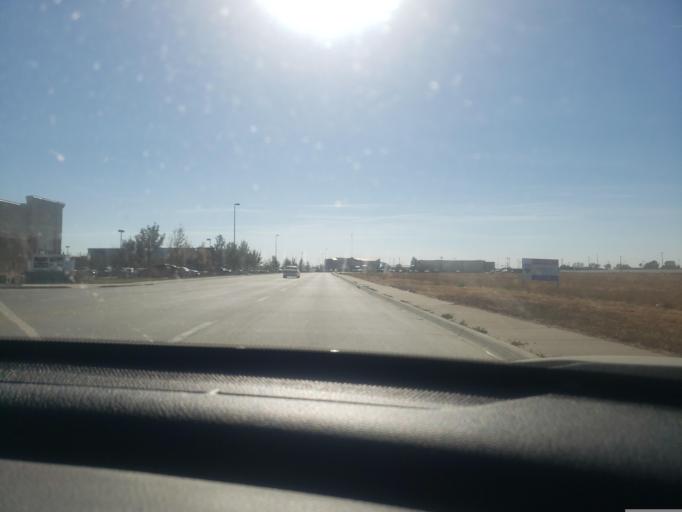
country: US
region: Kansas
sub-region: Finney County
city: Garden City
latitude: 37.9799
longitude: -100.8367
